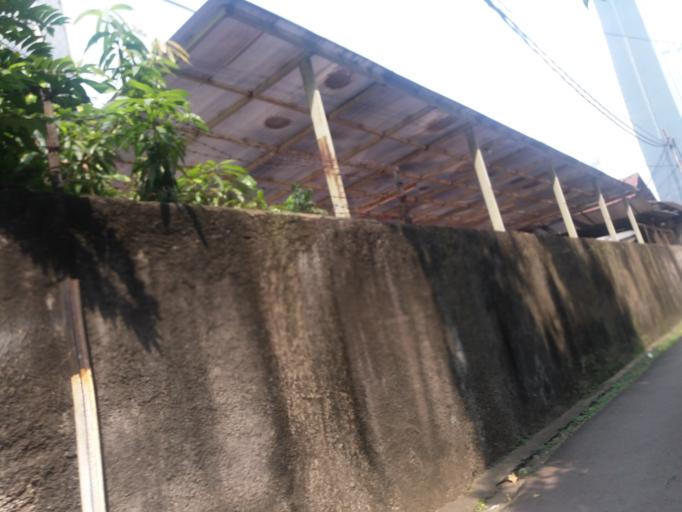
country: ID
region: Jakarta Raya
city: Jakarta
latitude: -6.2215
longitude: 106.8180
